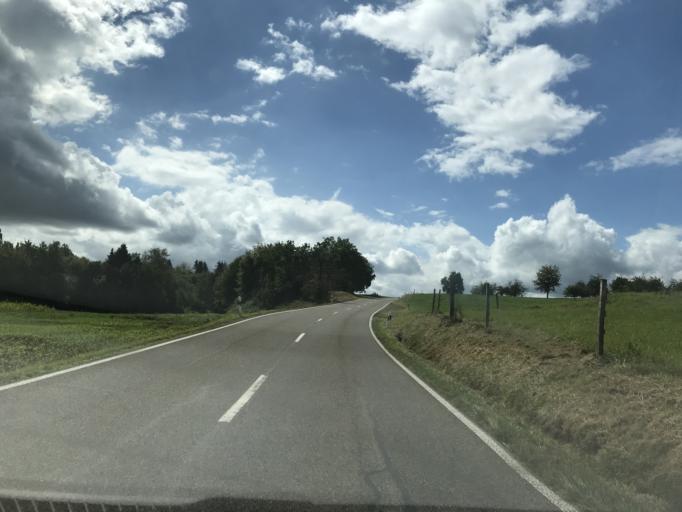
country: DE
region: Baden-Wuerttemberg
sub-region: Freiburg Region
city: Maulburg
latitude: 47.6229
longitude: 7.7691
